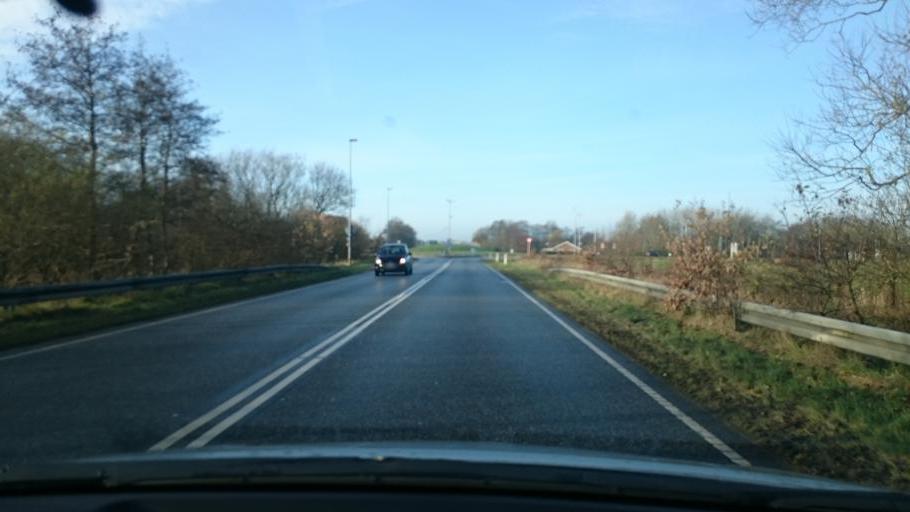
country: DK
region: South Denmark
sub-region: Esbjerg Kommune
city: Ribe
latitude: 55.3201
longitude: 8.7626
